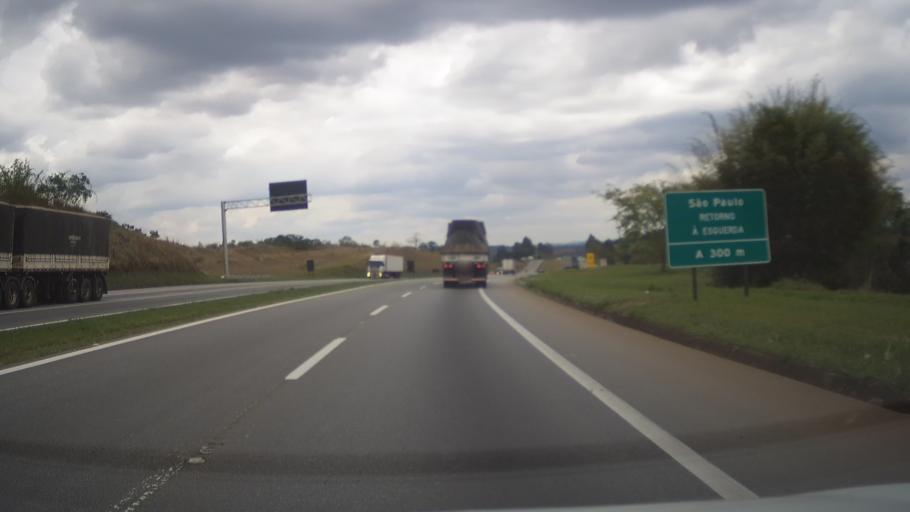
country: BR
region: Minas Gerais
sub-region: Tres Coracoes
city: Tres Coracoes
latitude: -21.4754
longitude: -45.2033
